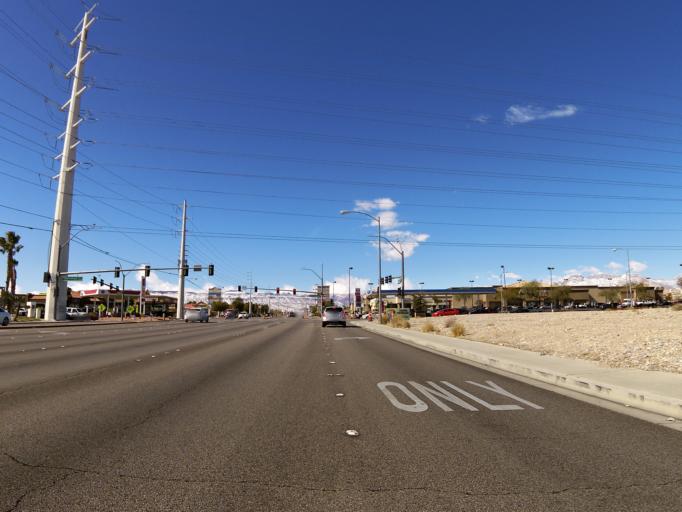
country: US
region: Nevada
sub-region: Clark County
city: Spring Valley
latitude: 36.1150
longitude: -115.2781
